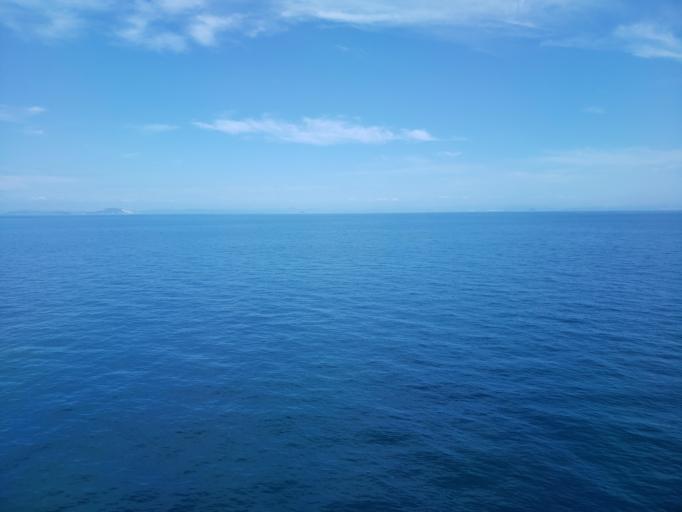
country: JP
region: Hyogo
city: Shirahamacho-usazakiminami
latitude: 34.5447
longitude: 134.7182
